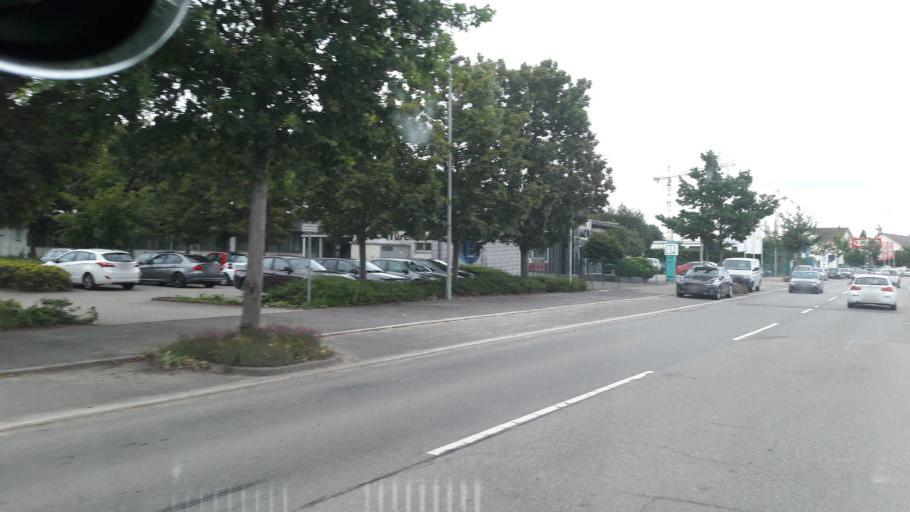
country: DE
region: Baden-Wuerttemberg
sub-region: Karlsruhe Region
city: Bruchsal
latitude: 49.1273
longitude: 8.5701
